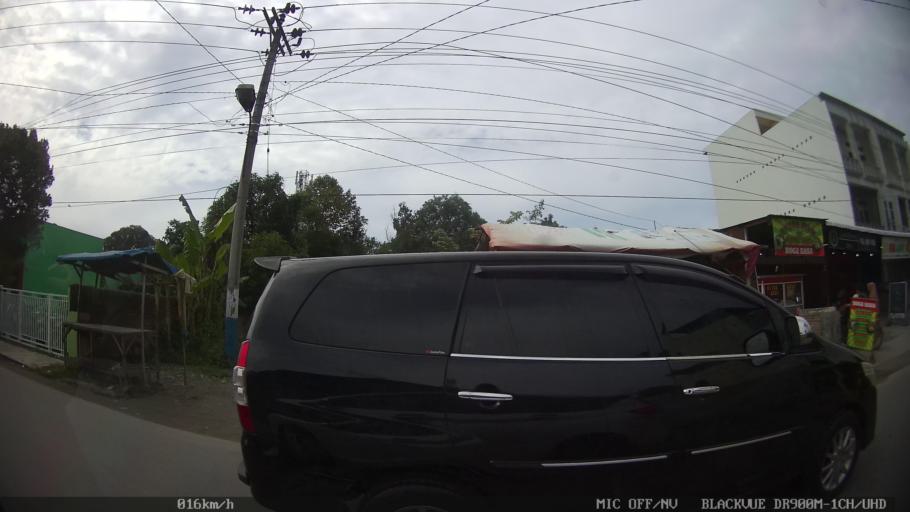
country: ID
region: North Sumatra
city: Medan
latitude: 3.6197
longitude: 98.7446
